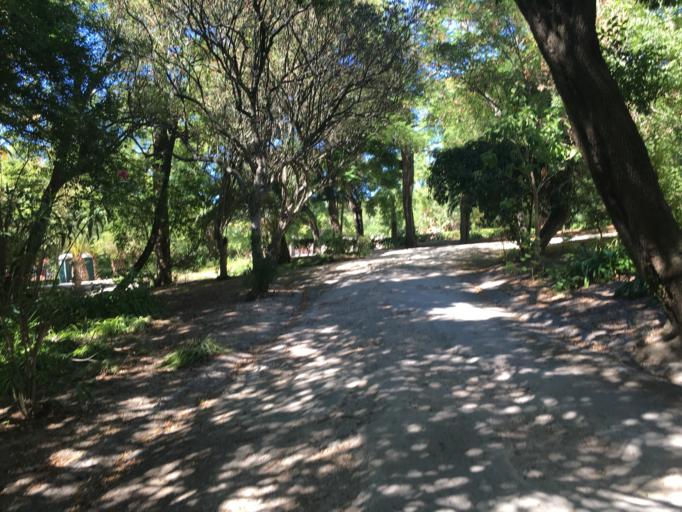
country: PT
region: Setubal
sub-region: Almada
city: Cacilhas
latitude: 38.7078
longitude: -9.1708
